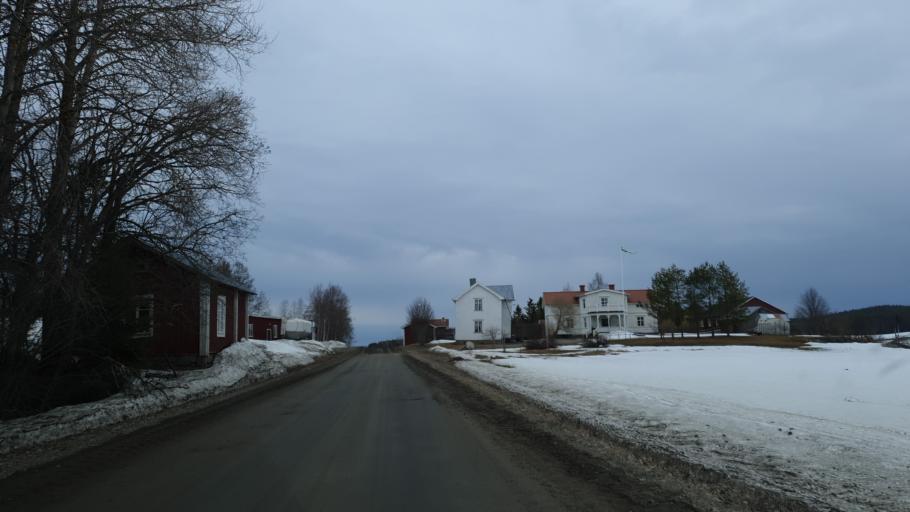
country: SE
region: Vaesterbotten
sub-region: Skelleftea Kommun
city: Burea
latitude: 64.3337
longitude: 21.1333
